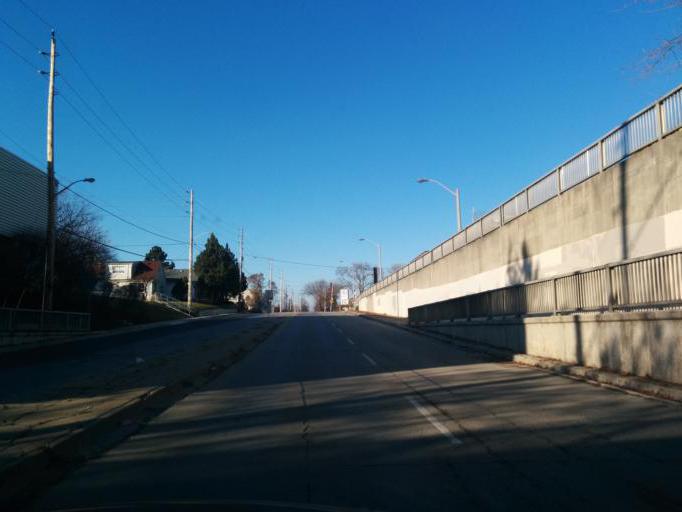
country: CA
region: Ontario
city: Etobicoke
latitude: 43.5991
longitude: -79.5313
